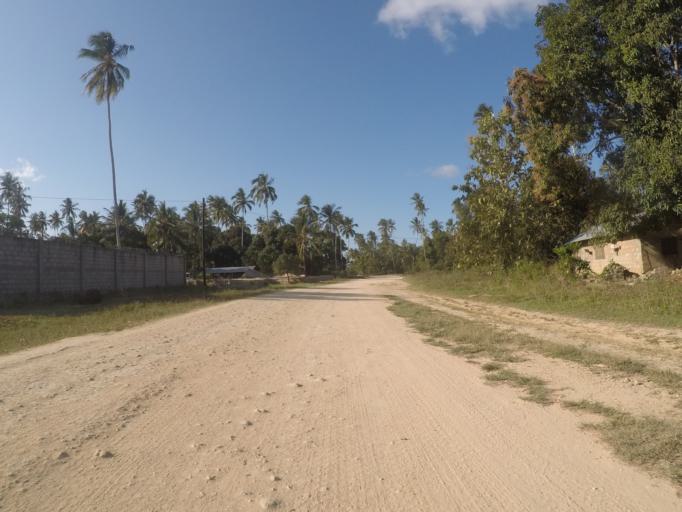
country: TZ
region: Zanzibar Central/South
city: Koani
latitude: -6.1645
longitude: 39.2867
